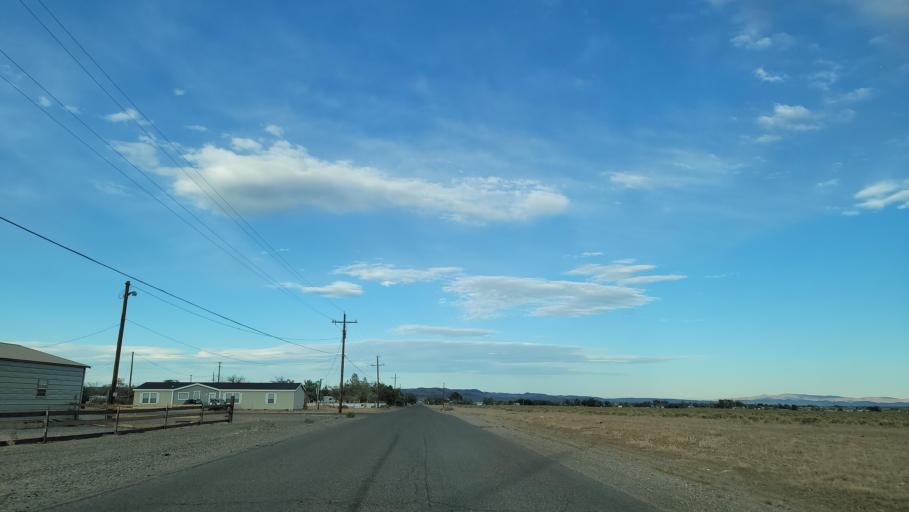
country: US
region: Nevada
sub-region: Lyon County
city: Silver Springs
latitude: 39.3899
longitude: -119.2481
